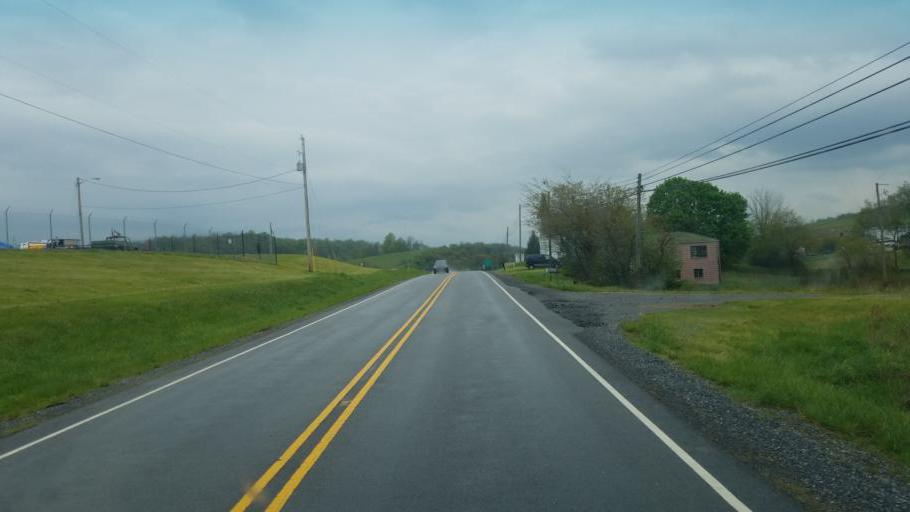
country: US
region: Virginia
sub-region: Wythe County
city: Rural Retreat
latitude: 36.8945
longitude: -81.3418
